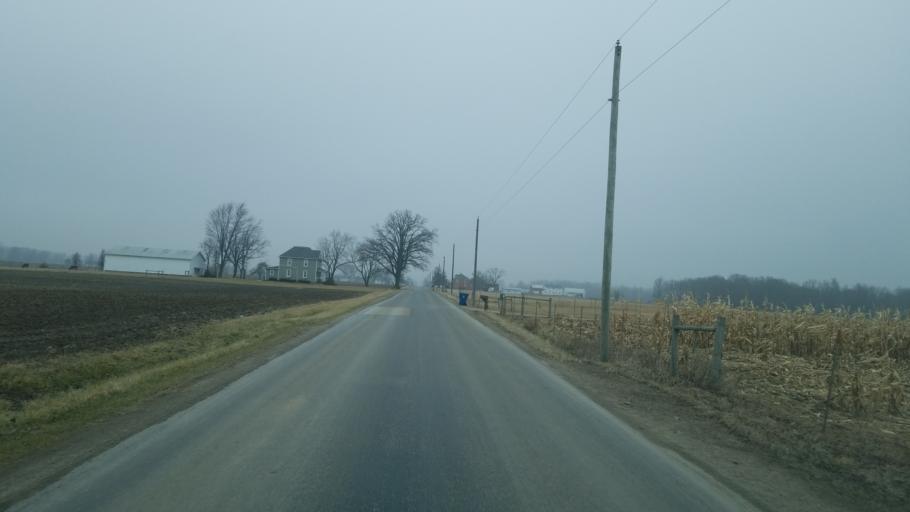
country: US
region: Indiana
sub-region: Adams County
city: Berne
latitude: 40.7221
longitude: -84.9751
